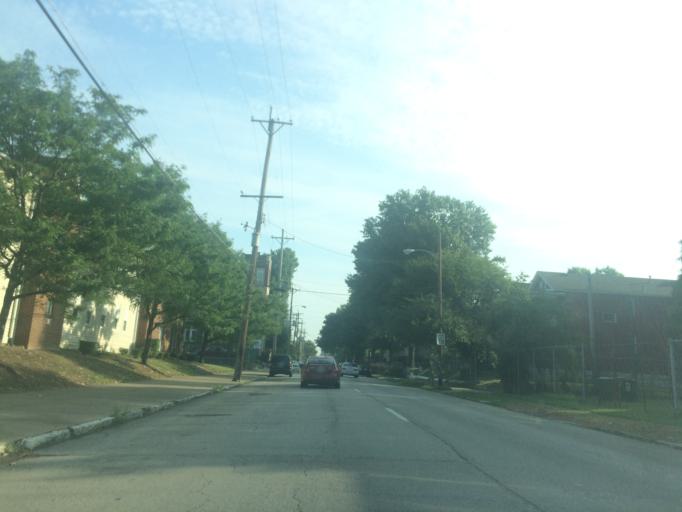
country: US
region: Kentucky
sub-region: Jefferson County
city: Louisville
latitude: 38.2354
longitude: -85.7473
